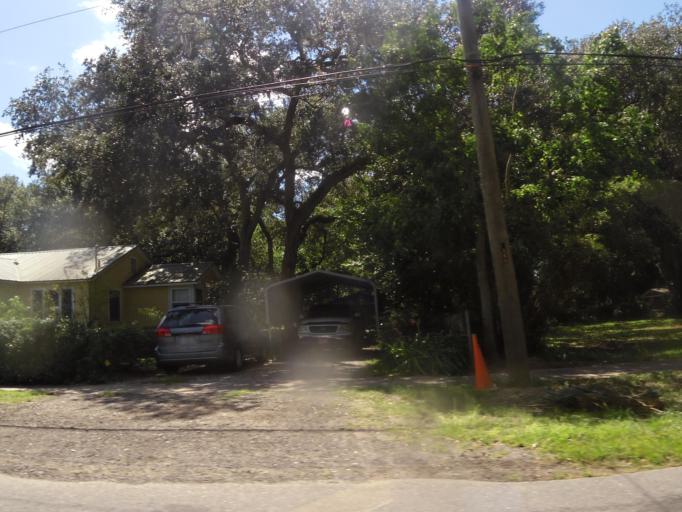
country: US
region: Florida
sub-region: Nassau County
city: Fernandina Beach
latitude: 30.6675
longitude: -81.4437
